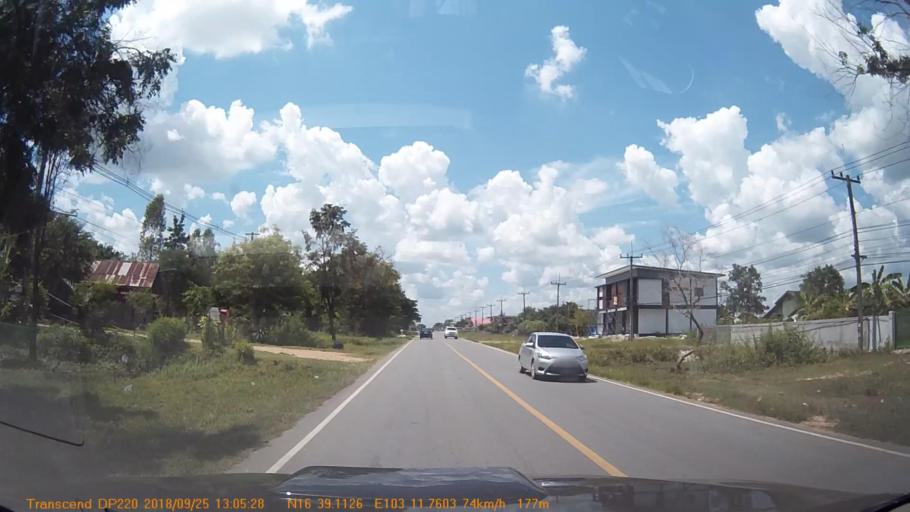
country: TH
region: Kalasin
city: Huai Mek
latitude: 16.6518
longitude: 103.1961
